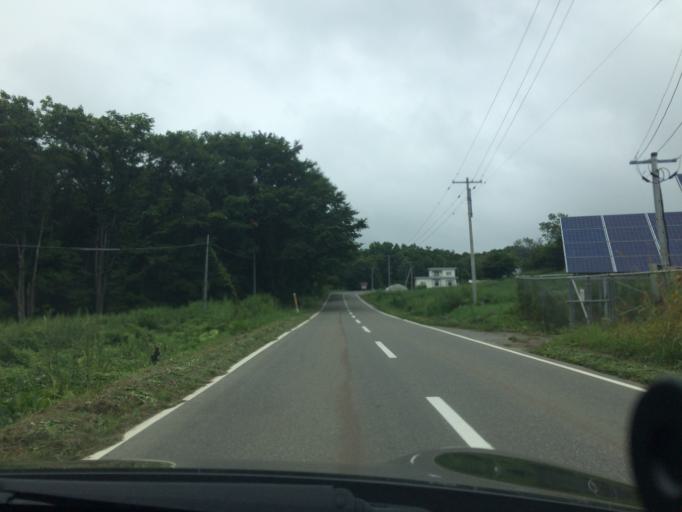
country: JP
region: Hokkaido
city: Otofuke
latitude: 42.9843
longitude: 143.0837
